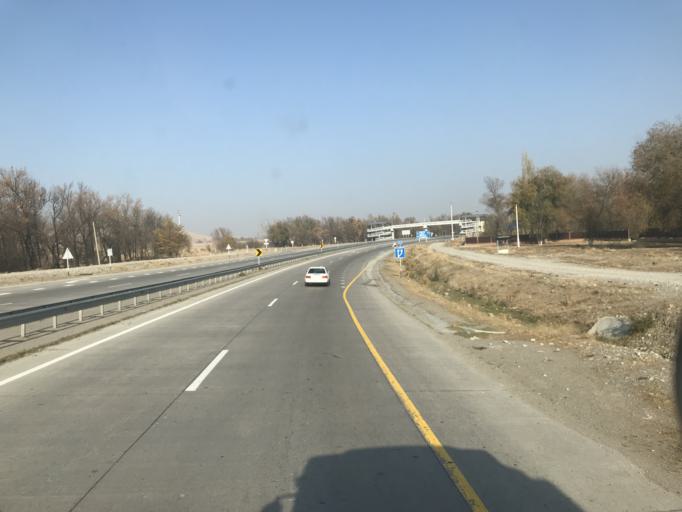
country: KZ
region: Ongtustik Qazaqstan
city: Sastobe
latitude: 42.5007
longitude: 69.9602
